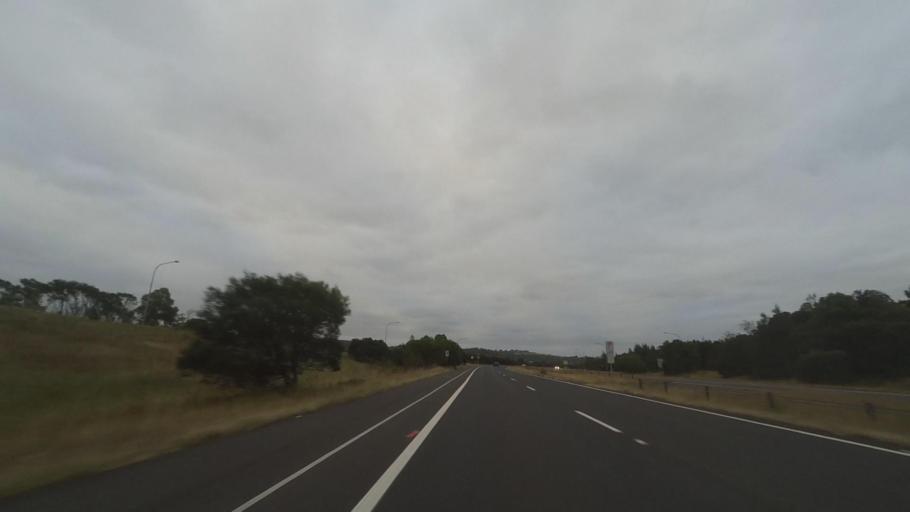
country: AU
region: New South Wales
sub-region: Shellharbour
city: Croom
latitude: -34.6151
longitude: 150.8373
